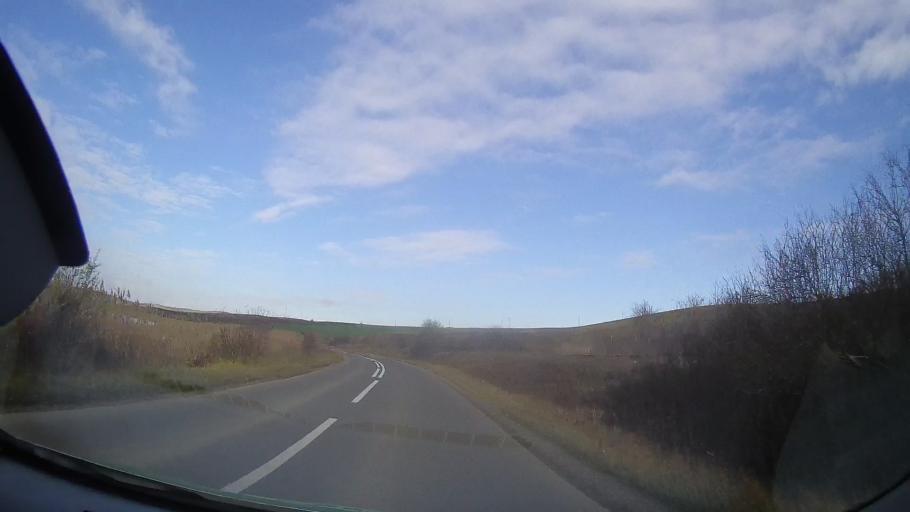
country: RO
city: Barza
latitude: 46.5599
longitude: 24.0988
